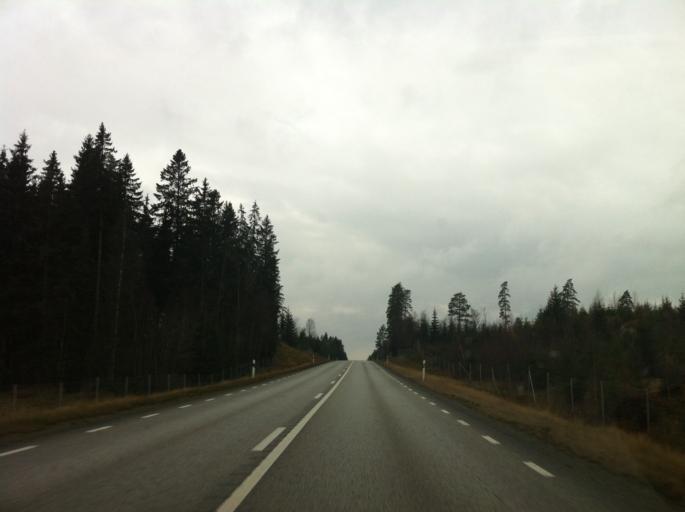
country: SE
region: Joenkoeping
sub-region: Savsjo Kommun
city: Saevsjoe
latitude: 57.3854
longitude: 14.6001
